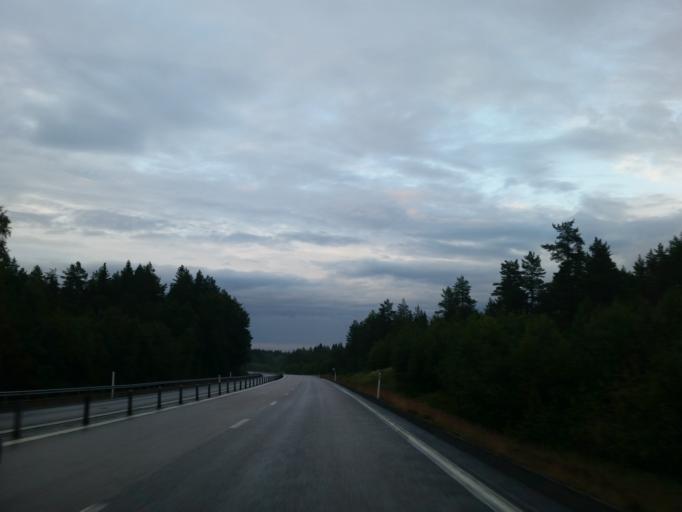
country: SE
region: Vaesterbotten
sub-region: Umea Kommun
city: Saevar
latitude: 63.9028
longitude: 20.5754
